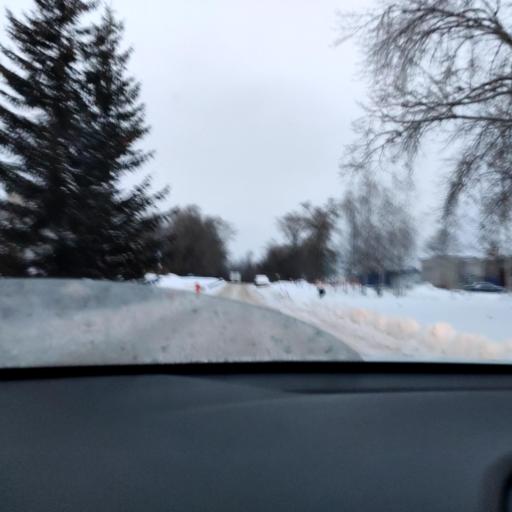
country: RU
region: Tatarstan
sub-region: Gorod Kazan'
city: Kazan
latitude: 55.8437
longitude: 49.0711
